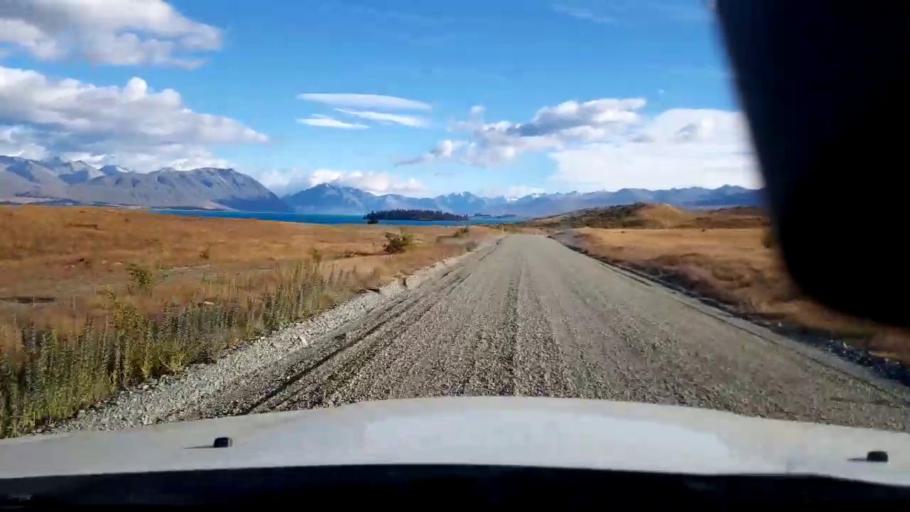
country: NZ
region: Canterbury
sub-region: Timaru District
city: Pleasant Point
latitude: -43.9716
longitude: 170.5135
